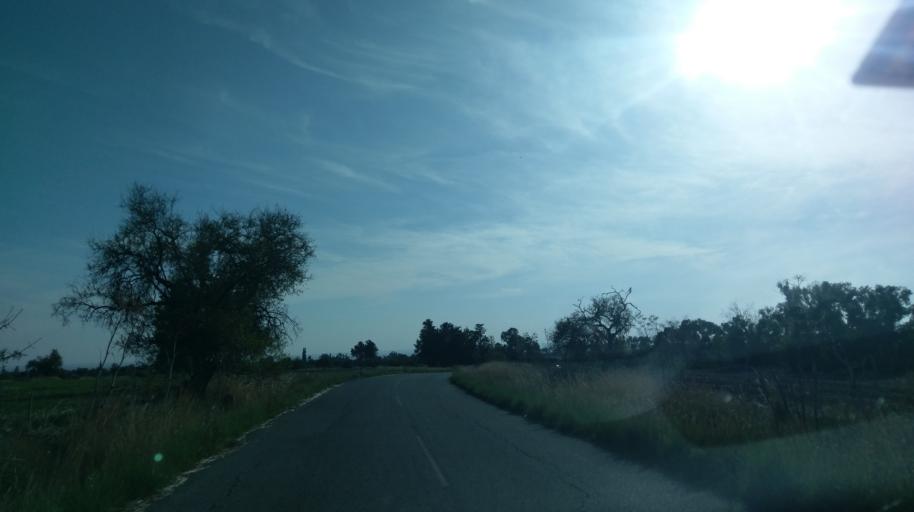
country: CY
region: Ammochostos
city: Lefkonoiko
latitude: 35.3060
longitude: 33.7475
